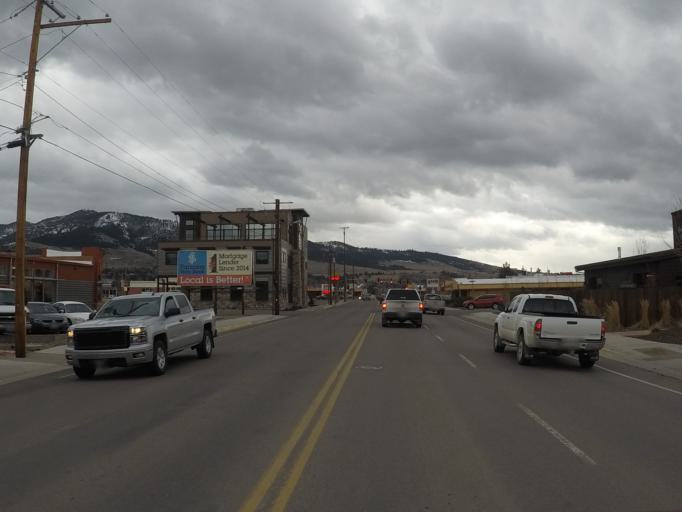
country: US
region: Montana
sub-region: Missoula County
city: Missoula
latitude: 46.8539
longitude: -114.0131
